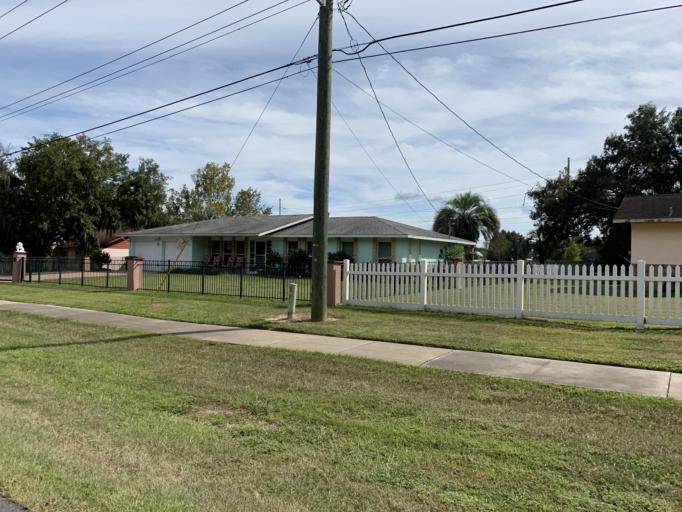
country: US
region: Florida
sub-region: Marion County
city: Ocala
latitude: 29.1642
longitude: -82.0851
